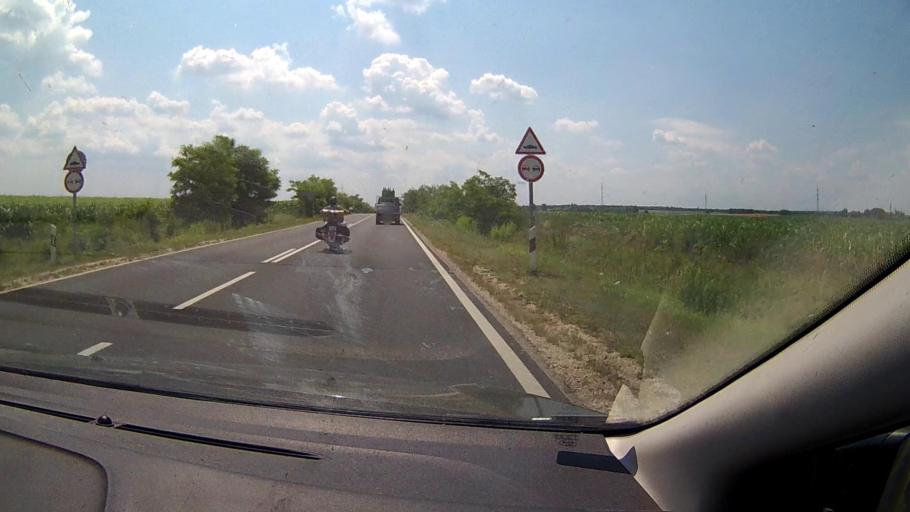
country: HU
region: Komarom-Esztergom
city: Tata
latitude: 47.6178
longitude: 18.3165
